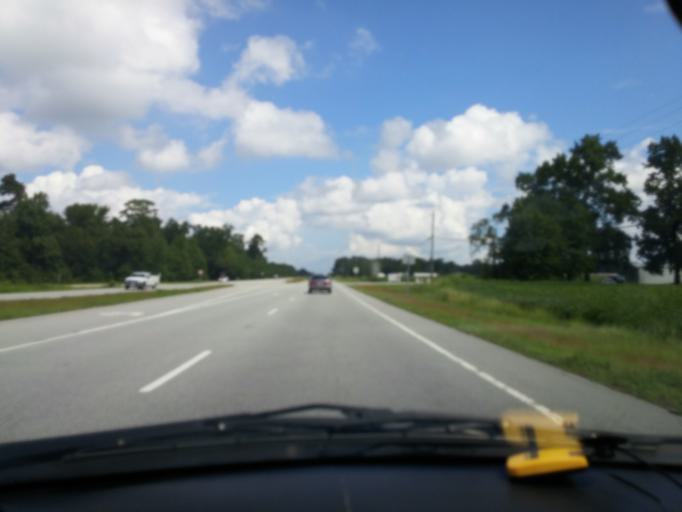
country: US
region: North Carolina
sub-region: Duplin County
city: Beulaville
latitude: 35.1094
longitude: -77.7192
